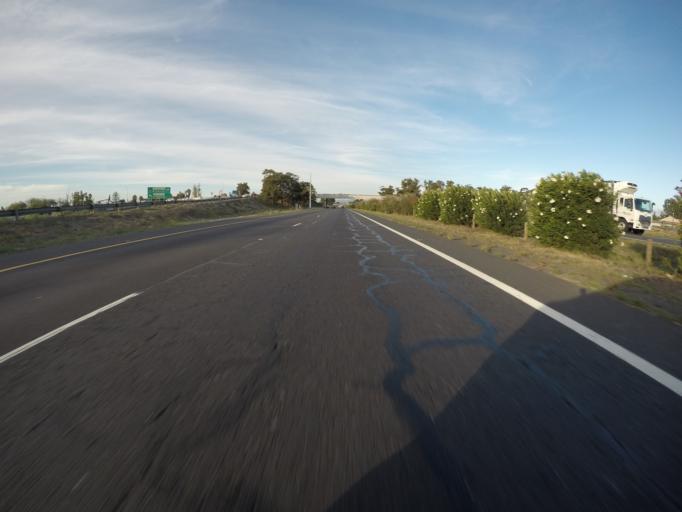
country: ZA
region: Western Cape
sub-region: City of Cape Town
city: Kraaifontein
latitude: -33.8460
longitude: 18.7137
